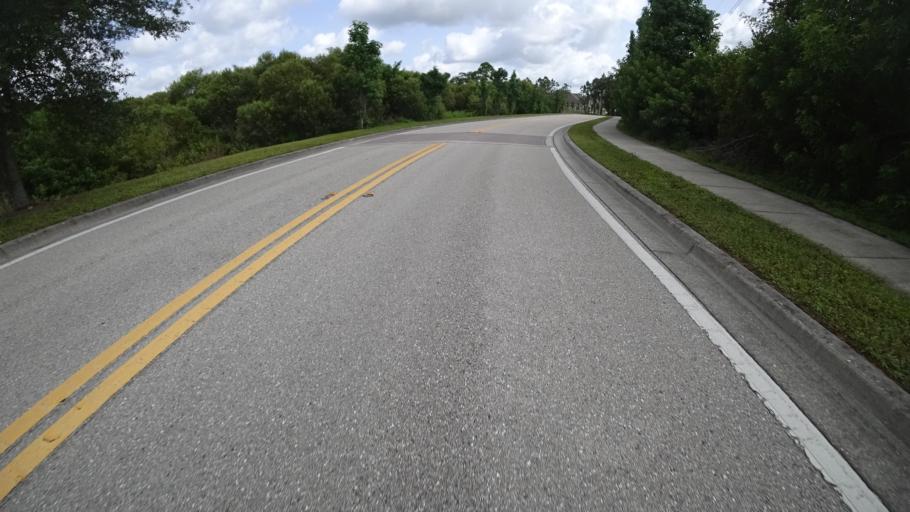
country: US
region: Florida
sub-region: Sarasota County
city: Desoto Lakes
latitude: 27.4191
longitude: -82.4549
